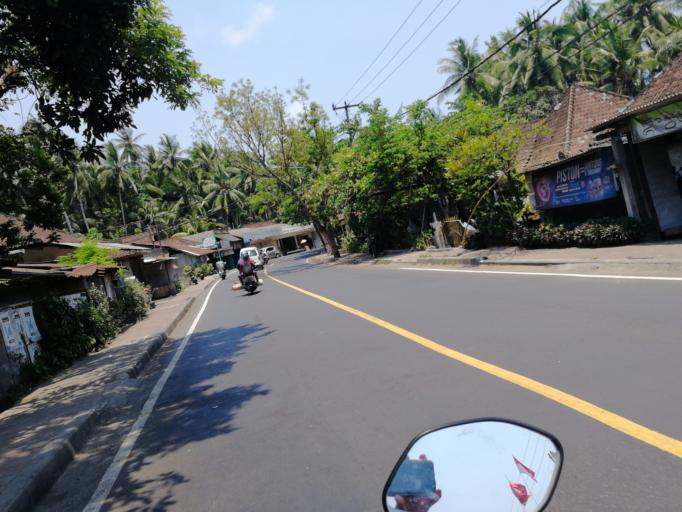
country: ID
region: Bali
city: Banjar Pegeringsingan
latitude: -8.4995
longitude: 115.5549
